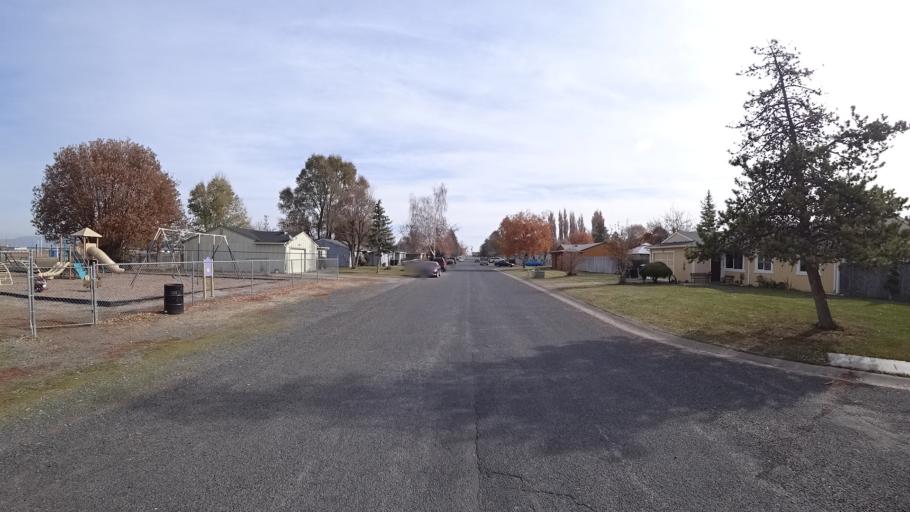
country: US
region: California
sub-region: Siskiyou County
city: Tulelake
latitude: 41.9481
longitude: -121.4745
